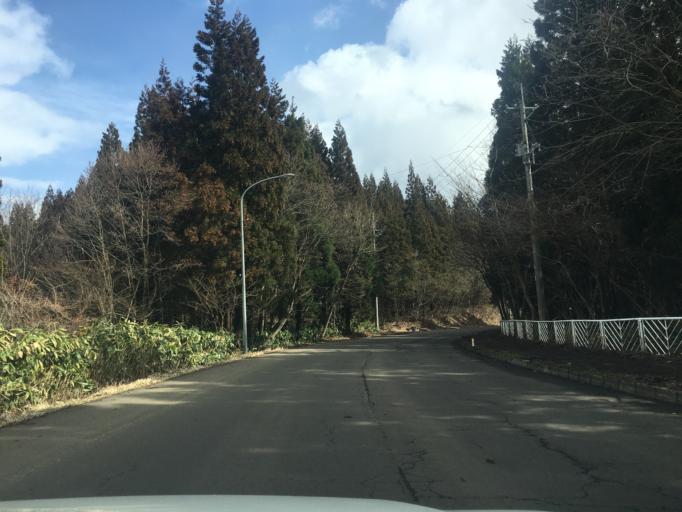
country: JP
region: Akita
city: Takanosu
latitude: 40.1894
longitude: 140.3446
